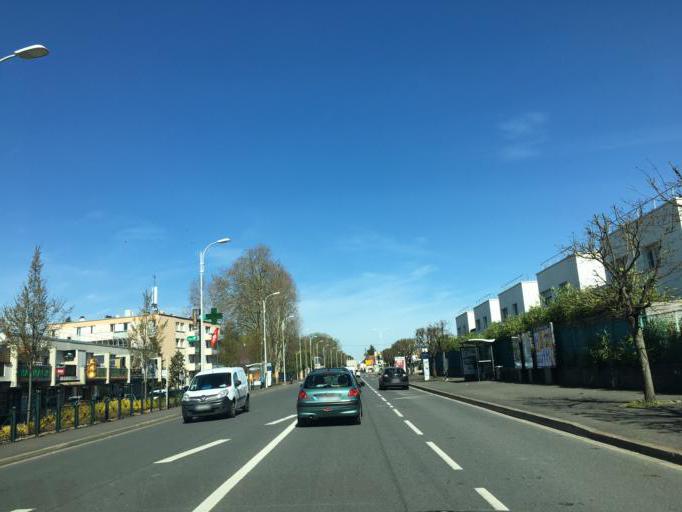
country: FR
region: Ile-de-France
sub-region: Departement de l'Essonne
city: Draveil
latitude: 48.6746
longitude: 2.4119
